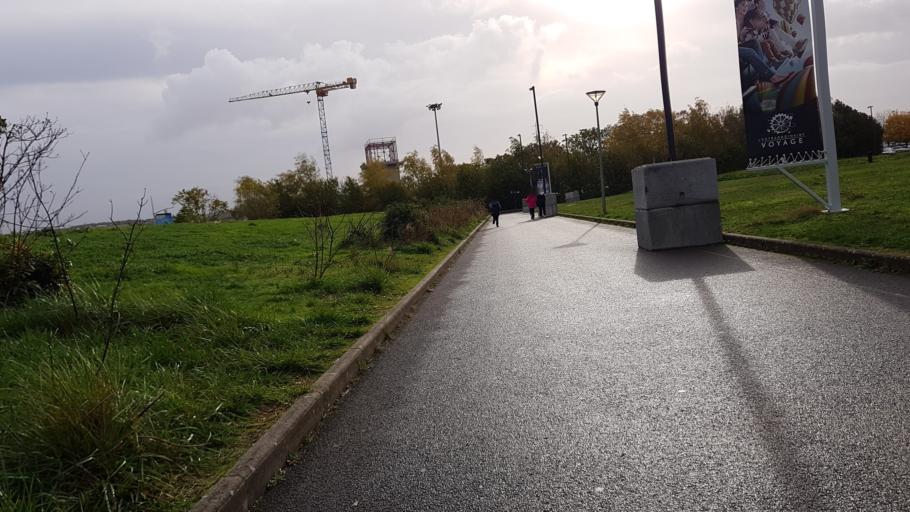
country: FR
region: Poitou-Charentes
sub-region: Departement de la Vienne
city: Chasseneuil-du-Poitou
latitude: 46.6667
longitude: 0.3654
